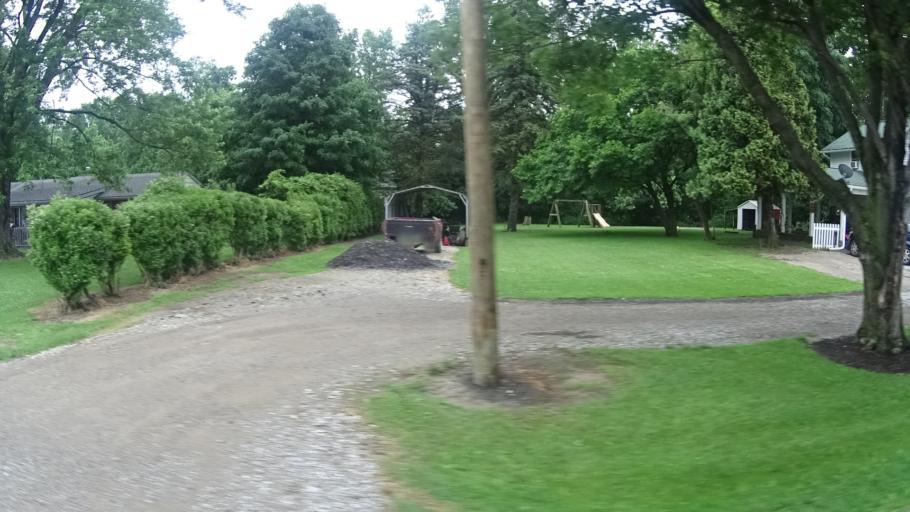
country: US
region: Ohio
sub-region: Erie County
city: Milan
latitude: 41.3211
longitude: -82.5965
